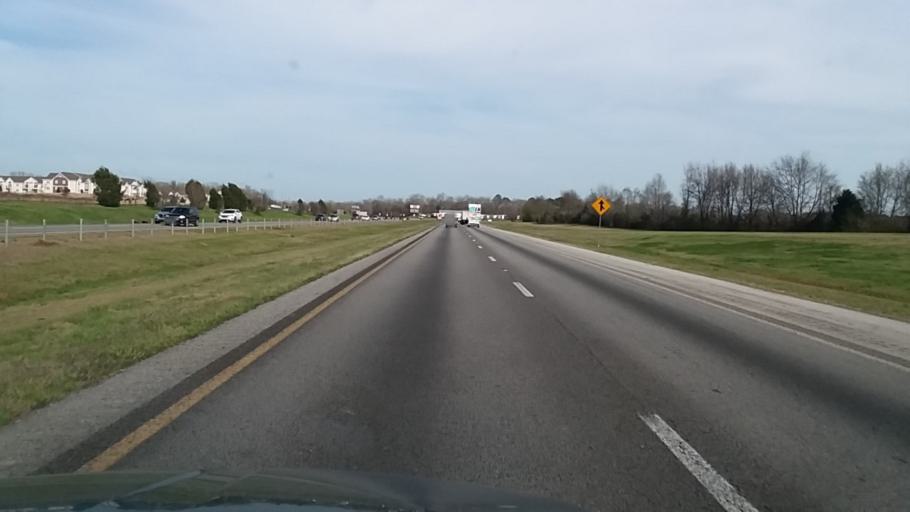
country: US
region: Alabama
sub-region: Morgan County
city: Priceville
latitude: 34.6310
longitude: -86.8787
